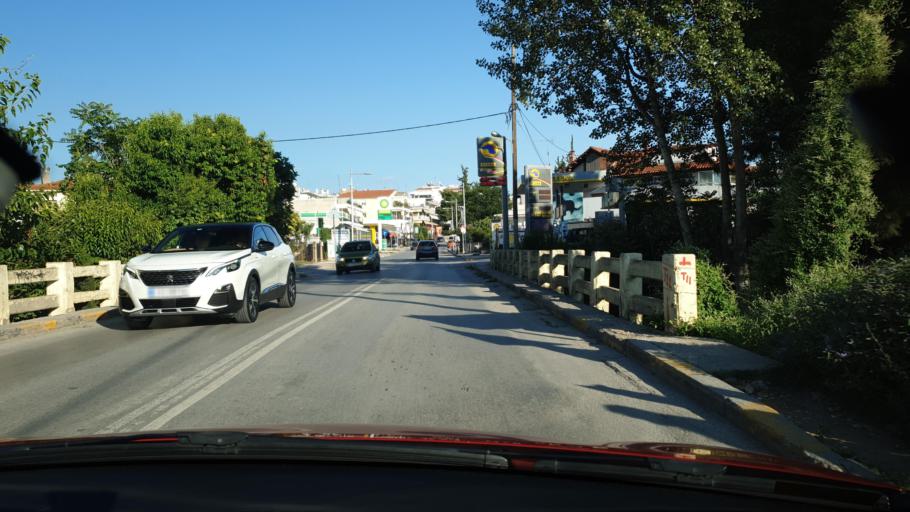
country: GR
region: Central Macedonia
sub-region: Nomos Thessalonikis
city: Pylaia
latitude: 40.6017
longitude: 22.9805
